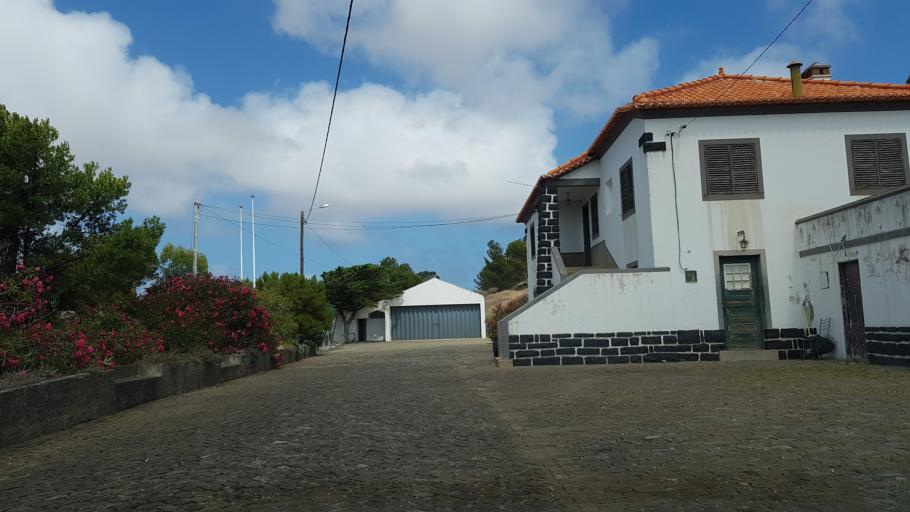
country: PT
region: Madeira
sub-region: Porto Santo
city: Vila de Porto Santo
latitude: 33.0666
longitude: -16.3348
